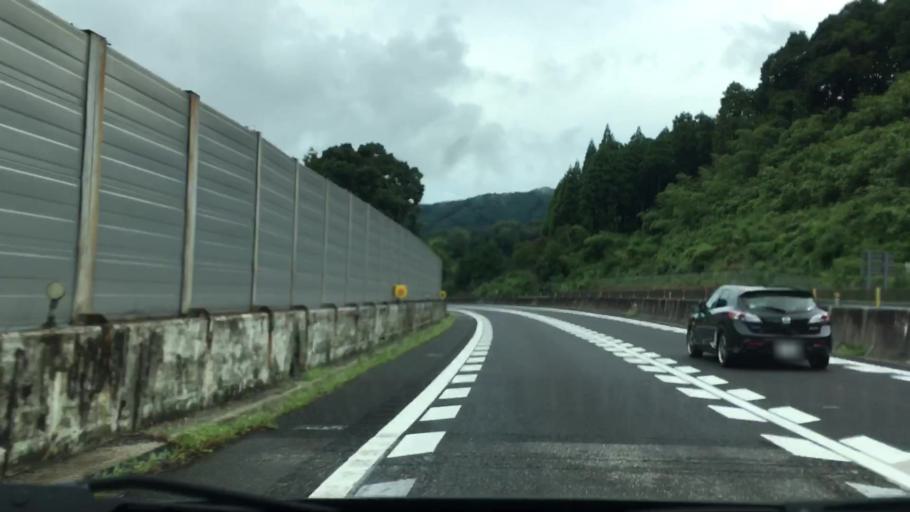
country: JP
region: Hyogo
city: Yamazakicho-nakabirose
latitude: 35.0461
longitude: 134.4518
